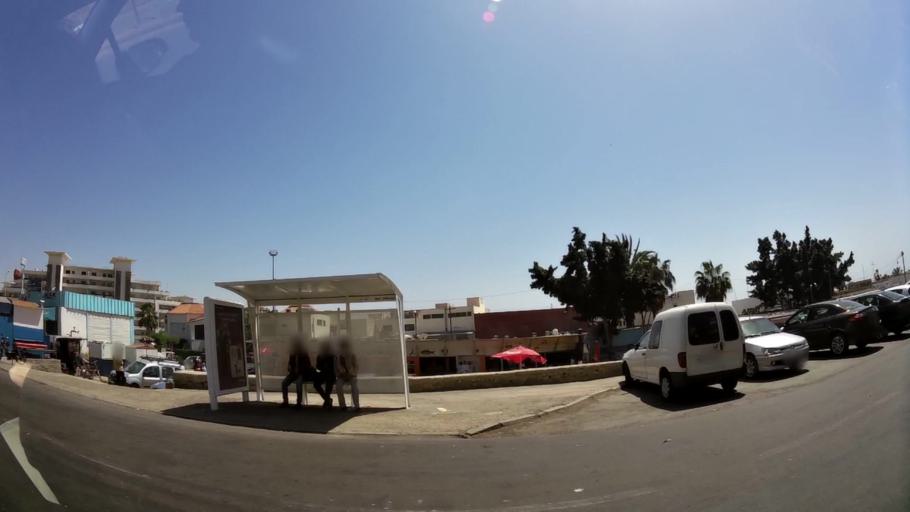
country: MA
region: Souss-Massa-Draa
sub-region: Agadir-Ida-ou-Tnan
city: Agadir
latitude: 30.4262
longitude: -9.6192
